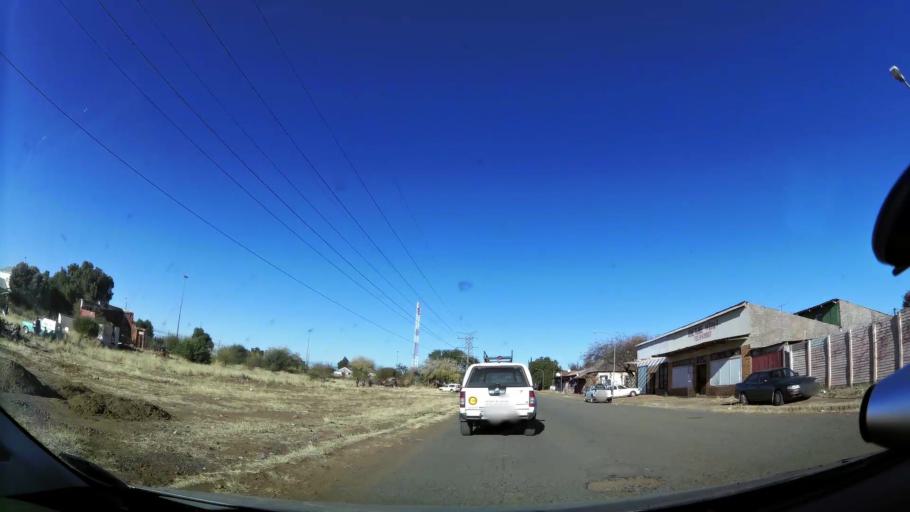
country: ZA
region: Northern Cape
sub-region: Frances Baard District Municipality
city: Kimberley
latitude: -28.7612
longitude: 24.7832
